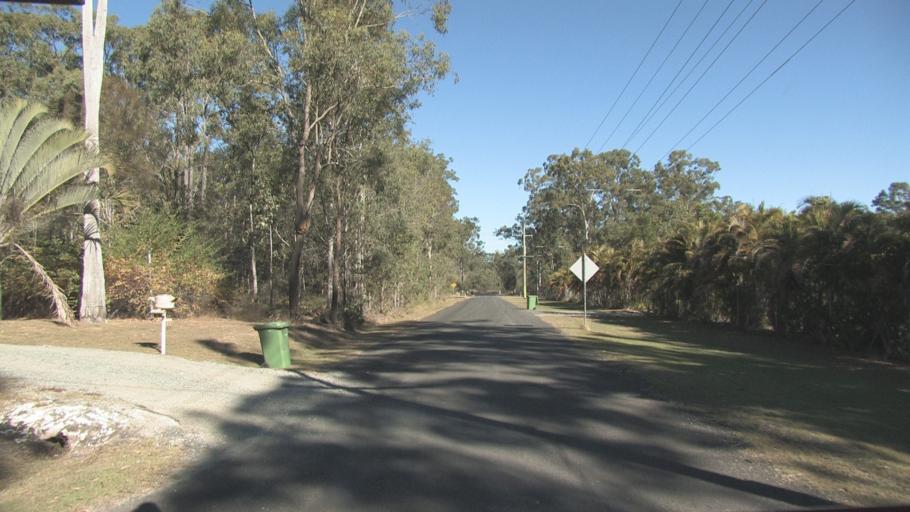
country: AU
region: Queensland
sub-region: Logan
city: Park Ridge South
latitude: -27.7300
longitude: 153.0025
